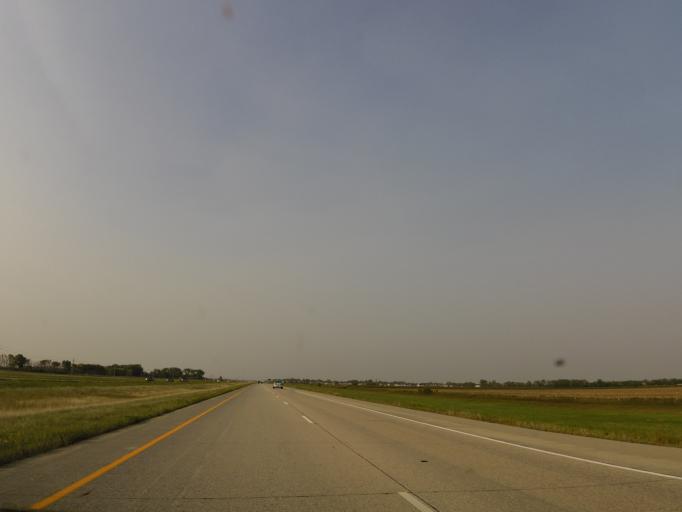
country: US
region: North Dakota
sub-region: Cass County
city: Horace
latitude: 46.7792
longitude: -96.8390
